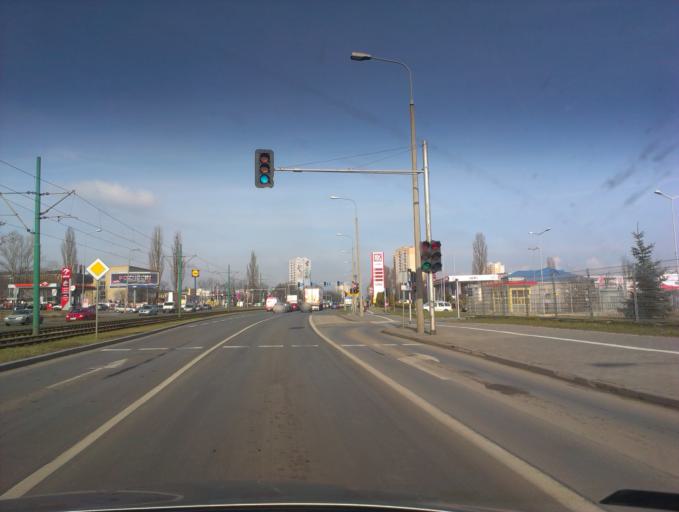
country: PL
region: Greater Poland Voivodeship
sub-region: Poznan
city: Poznan
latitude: 52.3823
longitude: 16.9438
